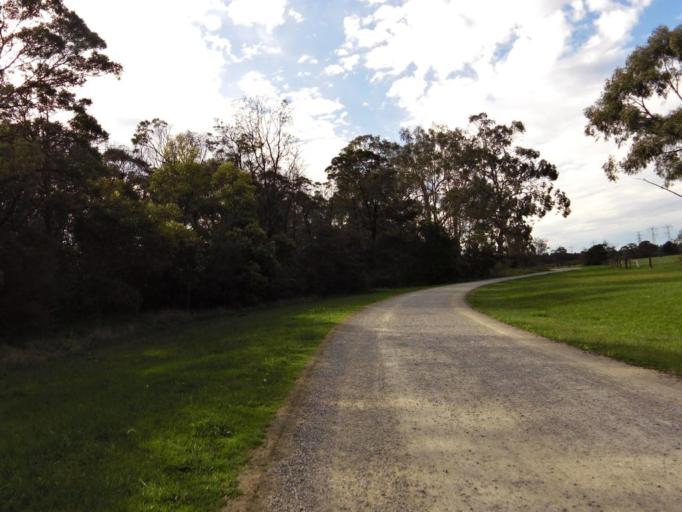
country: AU
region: Victoria
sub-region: Knox
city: Wantirna South
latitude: -37.8924
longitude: 145.2008
